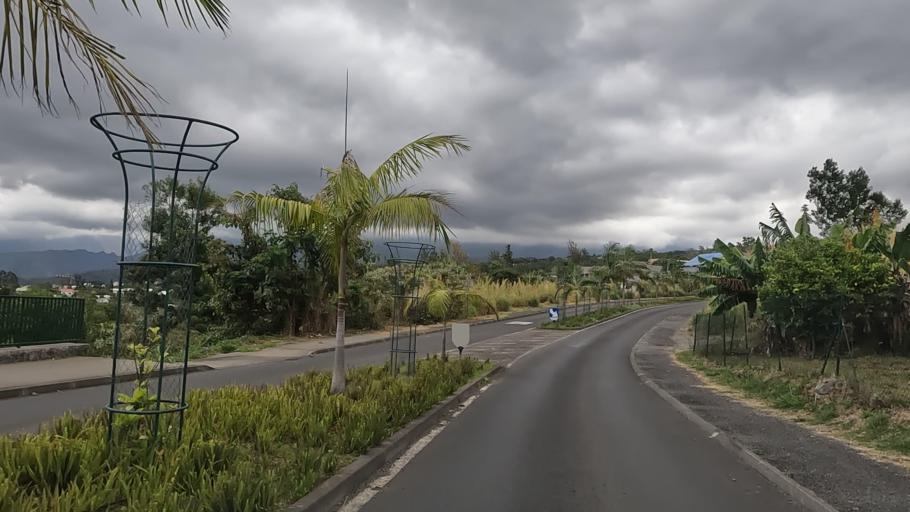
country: RE
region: Reunion
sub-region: Reunion
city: Le Tampon
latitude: -21.2664
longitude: 55.5123
